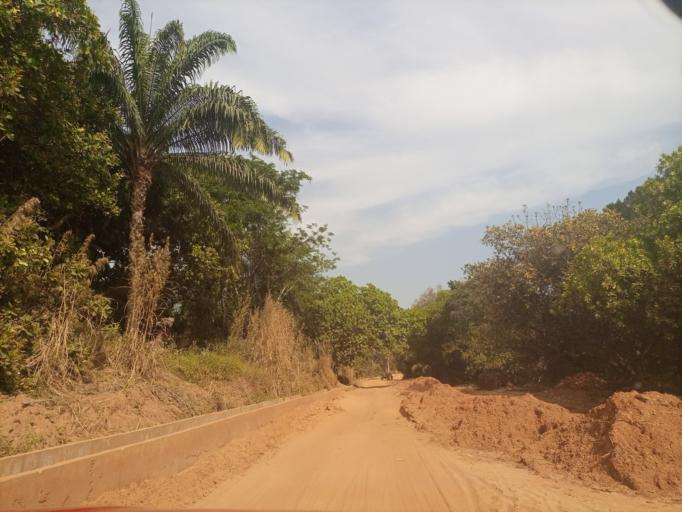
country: NG
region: Enugu
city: Opi
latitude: 6.8102
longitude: 7.5230
